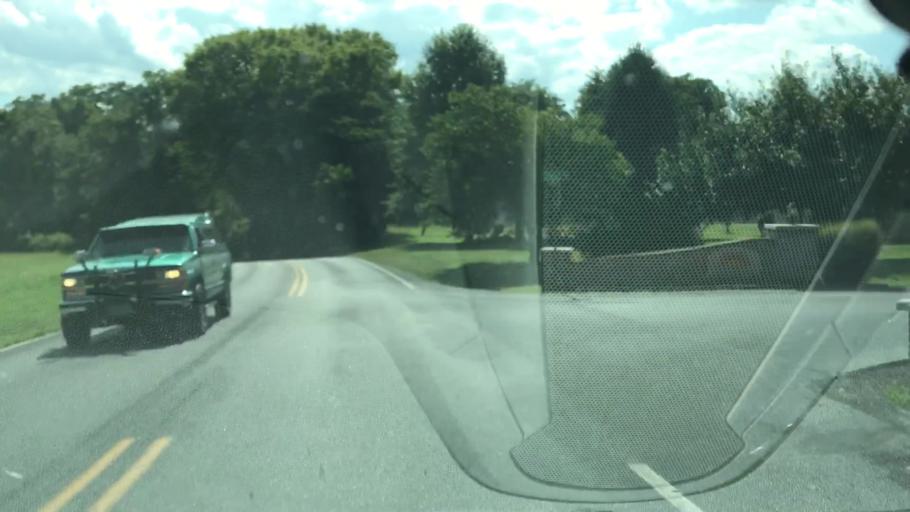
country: US
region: Pennsylvania
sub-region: Dauphin County
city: Middletown
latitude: 40.1679
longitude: -76.7120
